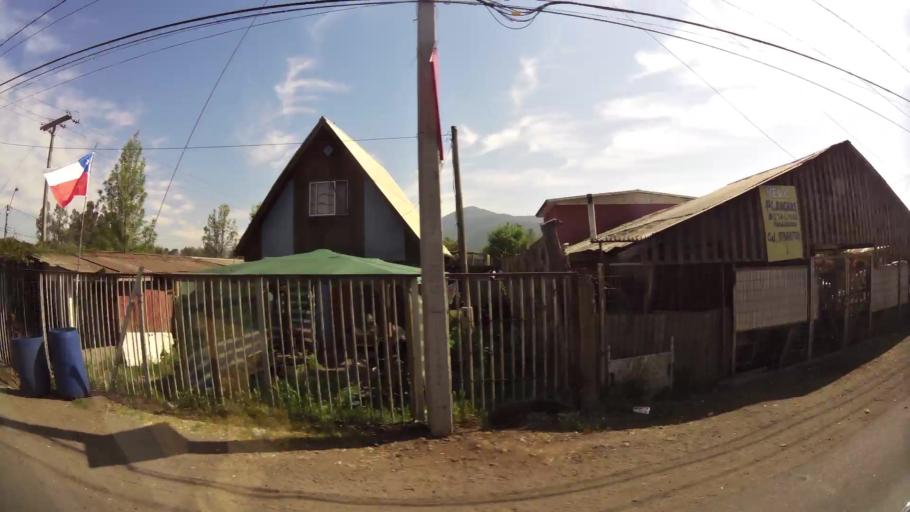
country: CL
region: Santiago Metropolitan
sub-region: Provincia de Talagante
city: Talagante
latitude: -33.6732
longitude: -70.9479
